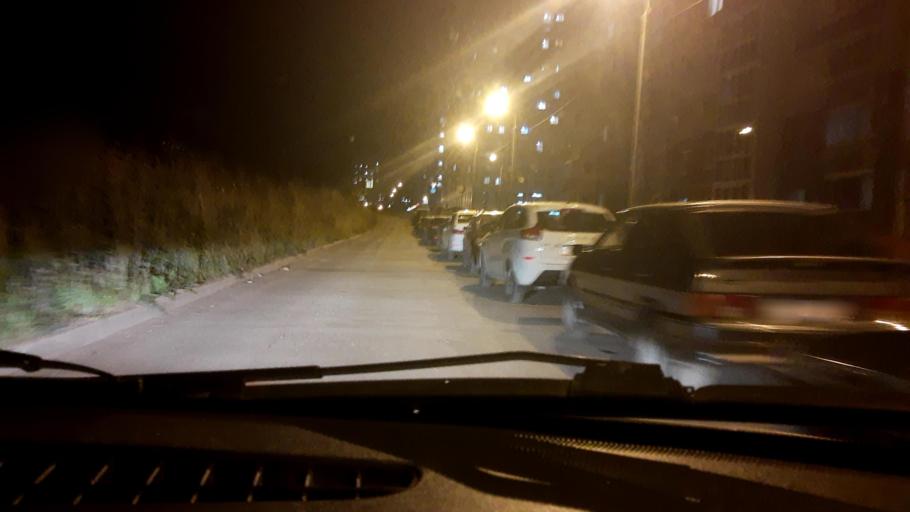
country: RU
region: Bashkortostan
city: Ufa
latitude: 54.7618
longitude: 56.0332
